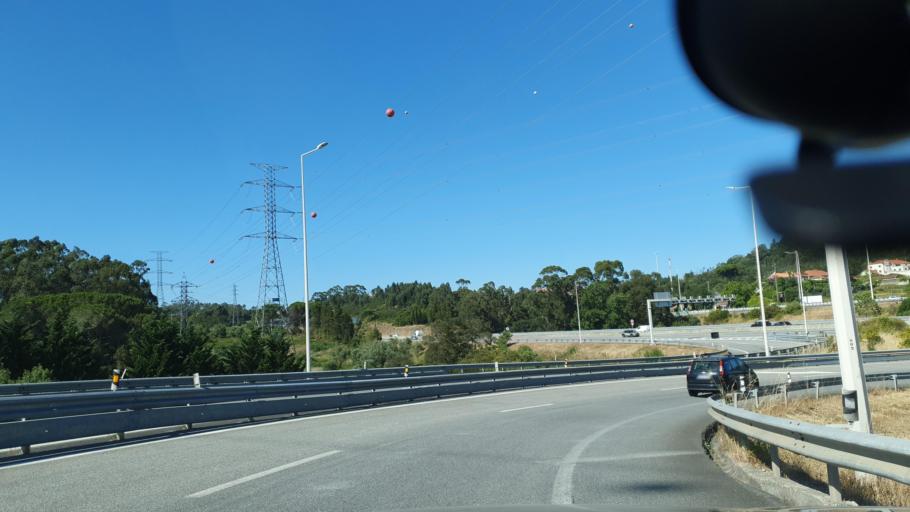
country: PT
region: Lisbon
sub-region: Sintra
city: Belas
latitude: 38.7868
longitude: -9.2436
